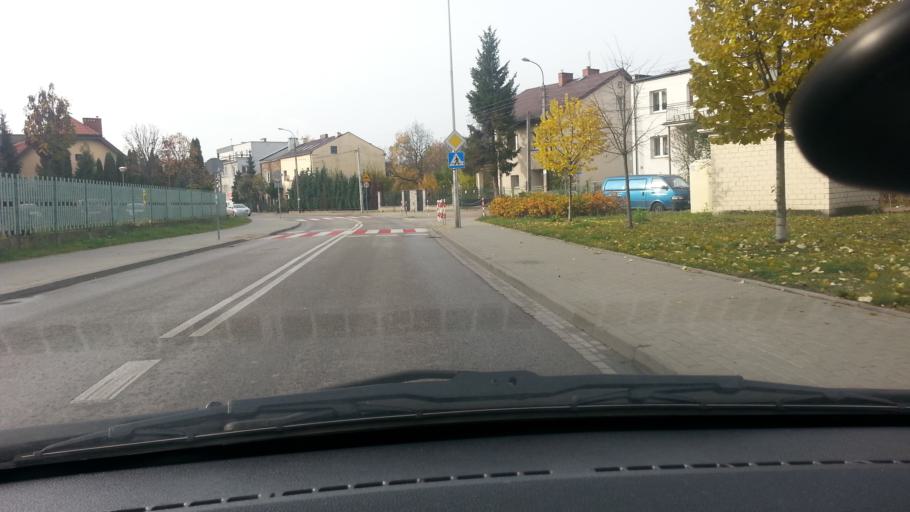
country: PL
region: Masovian Voivodeship
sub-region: Warszawa
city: Ursus
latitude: 52.1991
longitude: 20.8998
